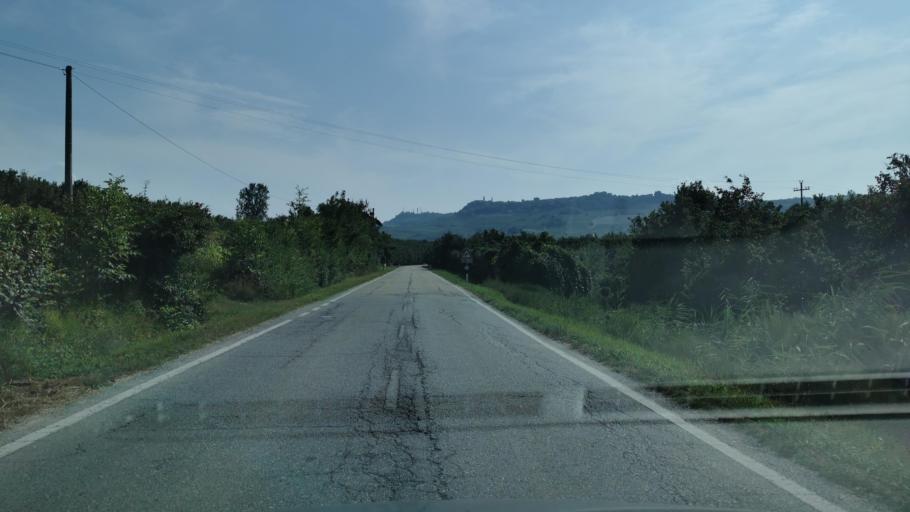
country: IT
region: Piedmont
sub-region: Provincia di Cuneo
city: Roddi
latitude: 44.6571
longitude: 7.9602
